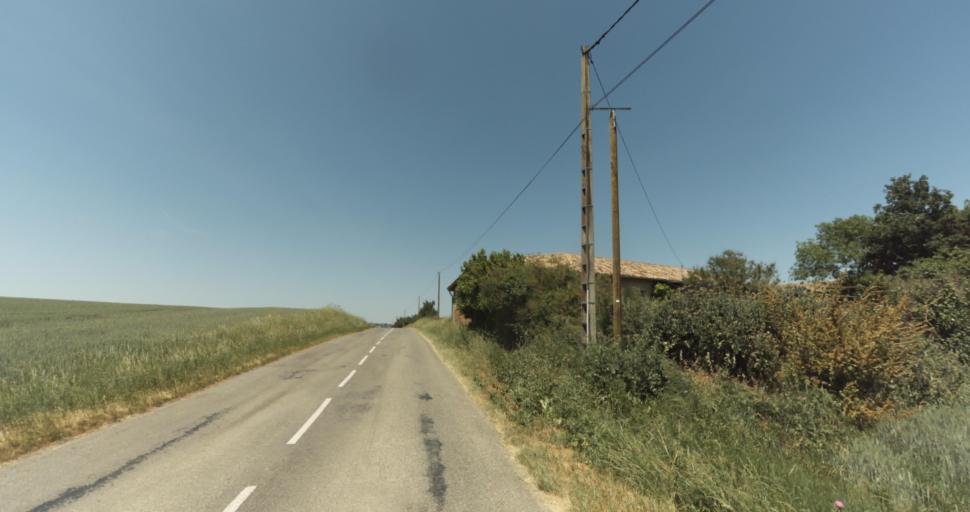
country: FR
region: Midi-Pyrenees
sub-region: Departement du Gers
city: Pujaudran
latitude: 43.6326
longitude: 1.1560
